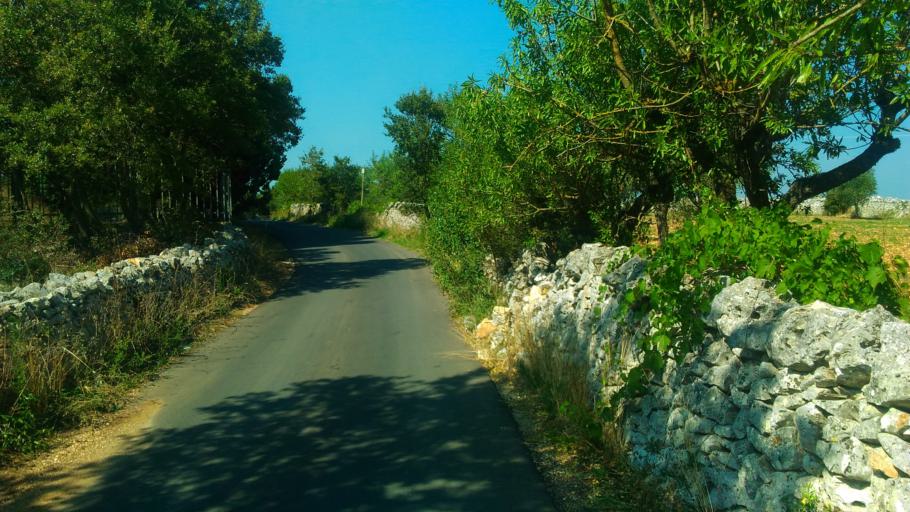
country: IT
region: Apulia
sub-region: Provincia di Bari
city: Alberobello
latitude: 40.8032
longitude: 17.1833
